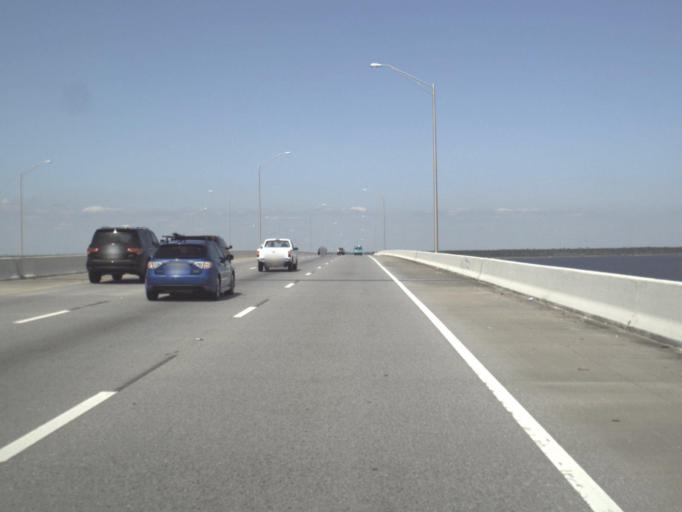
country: US
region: Florida
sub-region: Escambia County
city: Ferry Pass
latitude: 30.5154
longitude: -87.1489
